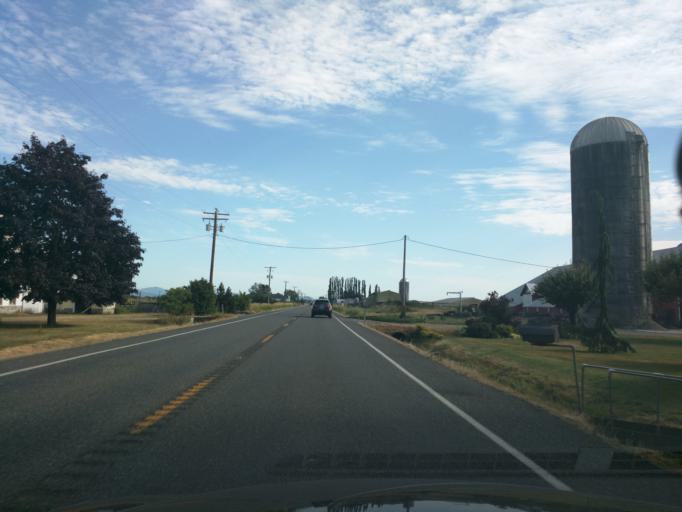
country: US
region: Washington
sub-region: Whatcom County
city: Lynden
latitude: 48.9859
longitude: -122.4852
